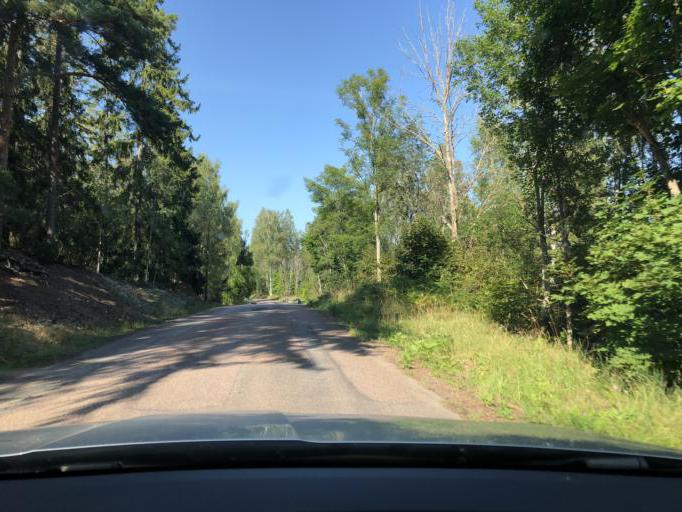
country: SE
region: Dalarna
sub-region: Hedemora Kommun
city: Hedemora
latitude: 60.3535
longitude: 15.9278
